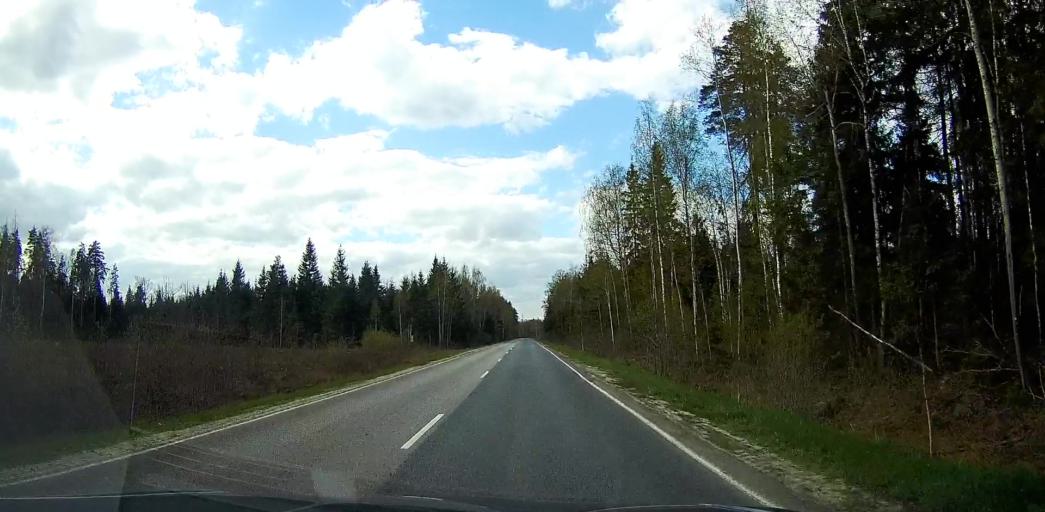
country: RU
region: Moskovskaya
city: Rakhmanovo
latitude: 55.6489
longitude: 38.6663
